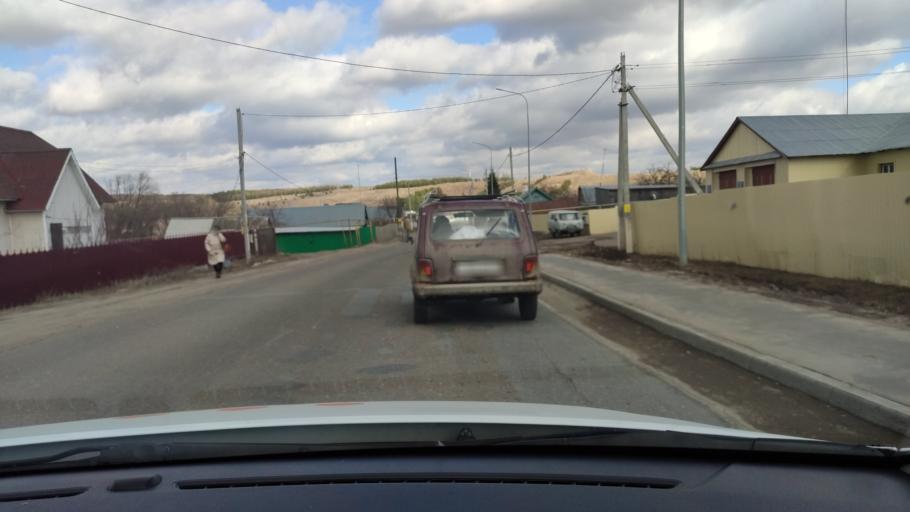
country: RU
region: Tatarstan
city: Vysokaya Gora
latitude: 56.1216
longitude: 49.1987
